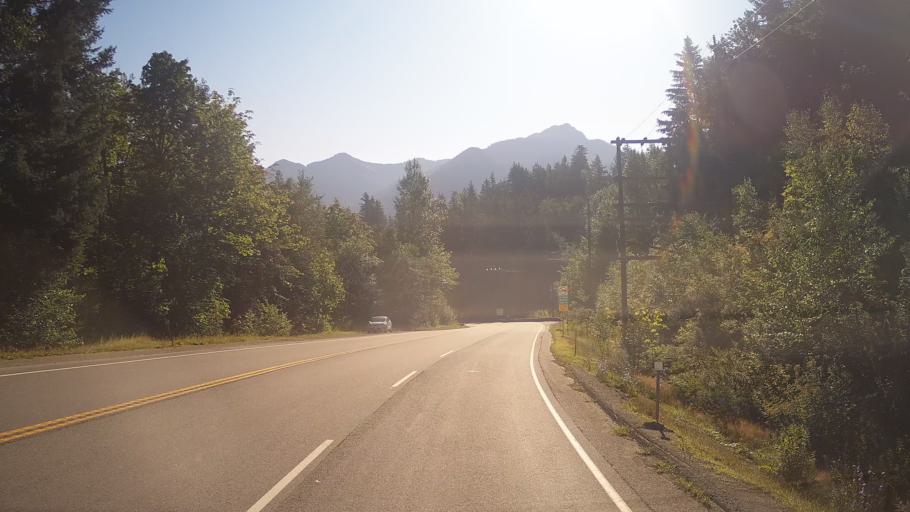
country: CA
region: British Columbia
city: Hope
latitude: 49.4084
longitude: -121.4504
